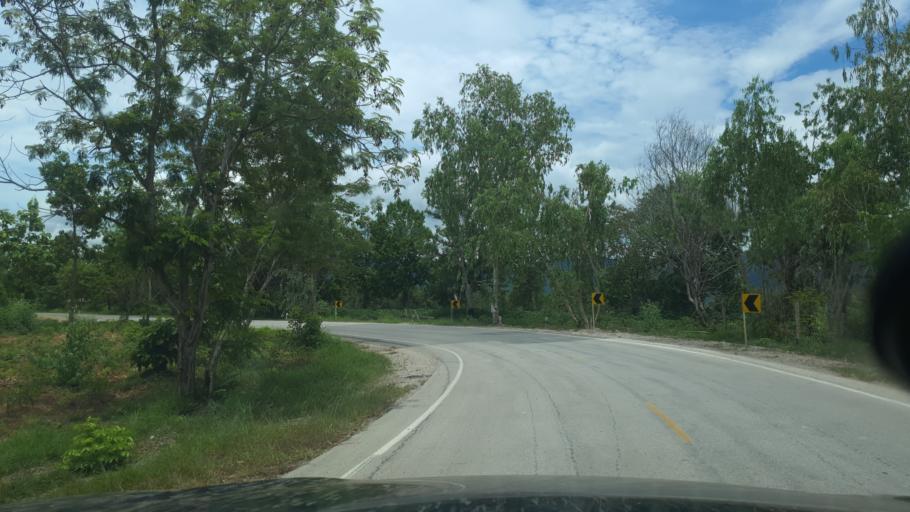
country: TH
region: Lampang
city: Sop Prap
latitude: 17.9135
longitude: 99.3970
